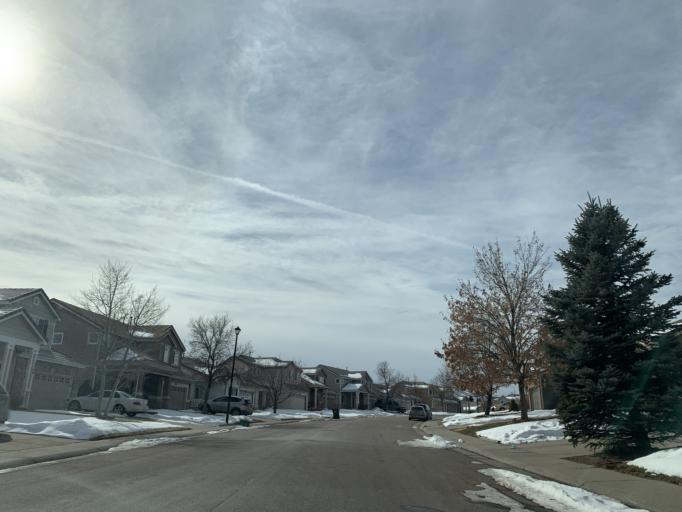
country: US
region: Colorado
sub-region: Douglas County
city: Carriage Club
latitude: 39.5260
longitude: -104.9327
